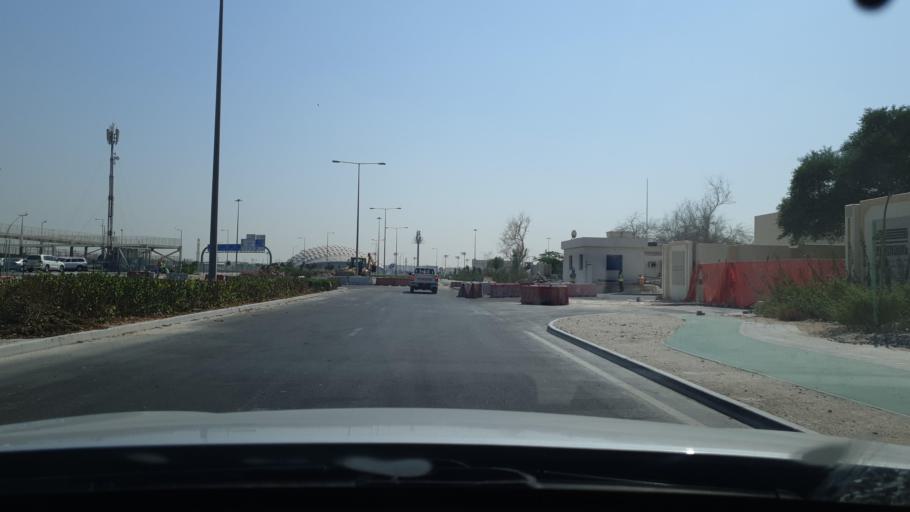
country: QA
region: Baladiyat ad Dawhah
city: Doha
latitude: 25.2305
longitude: 51.5283
